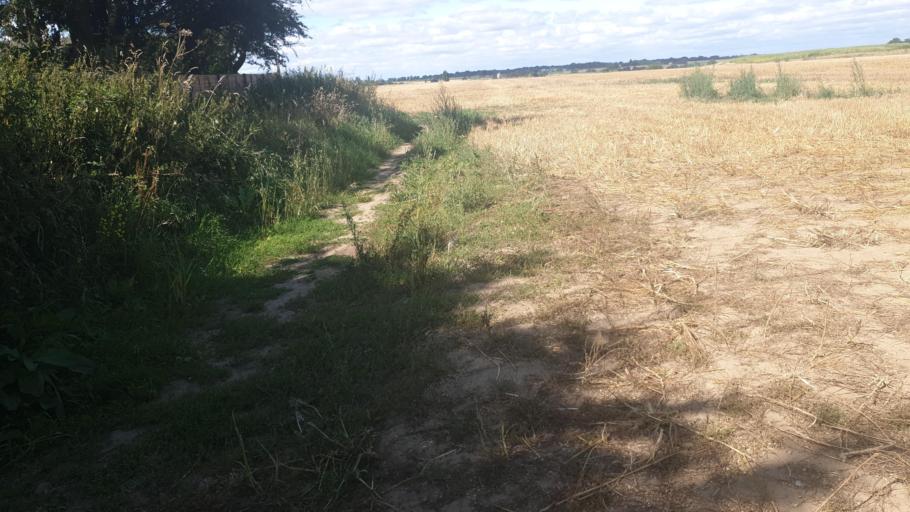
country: GB
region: England
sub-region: Essex
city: Dovercourt
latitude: 51.9185
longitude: 1.2214
